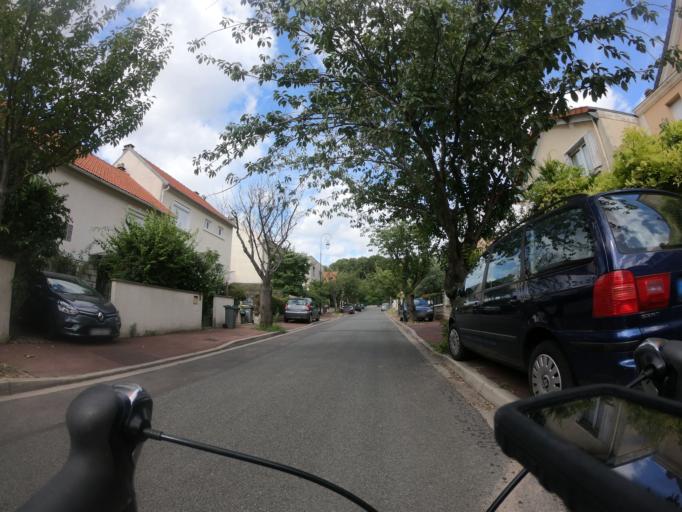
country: FR
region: Ile-de-France
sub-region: Departement des Hauts-de-Seine
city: Antony
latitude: 48.7579
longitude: 2.2947
